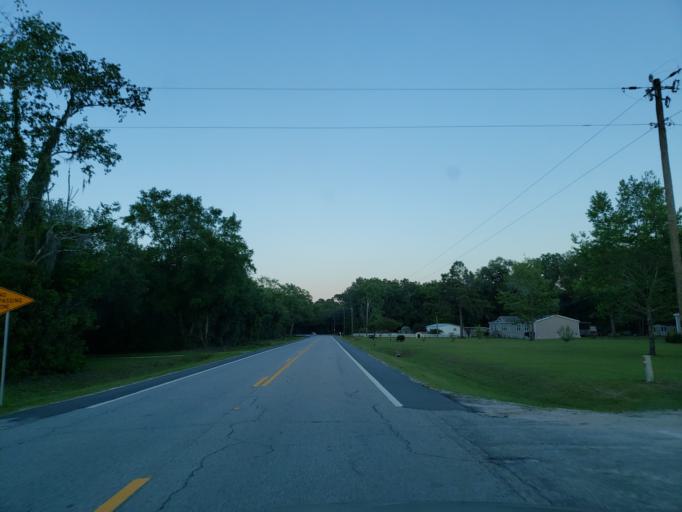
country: US
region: Florida
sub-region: Hamilton County
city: Jasper
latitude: 30.5543
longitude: -83.1094
